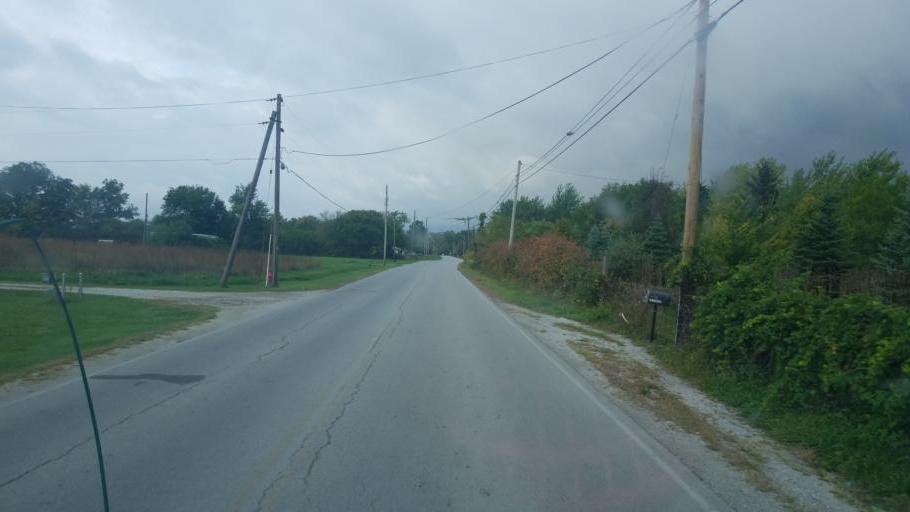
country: US
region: Ohio
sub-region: Wood County
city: North Baltimore
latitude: 41.1824
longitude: -83.6525
